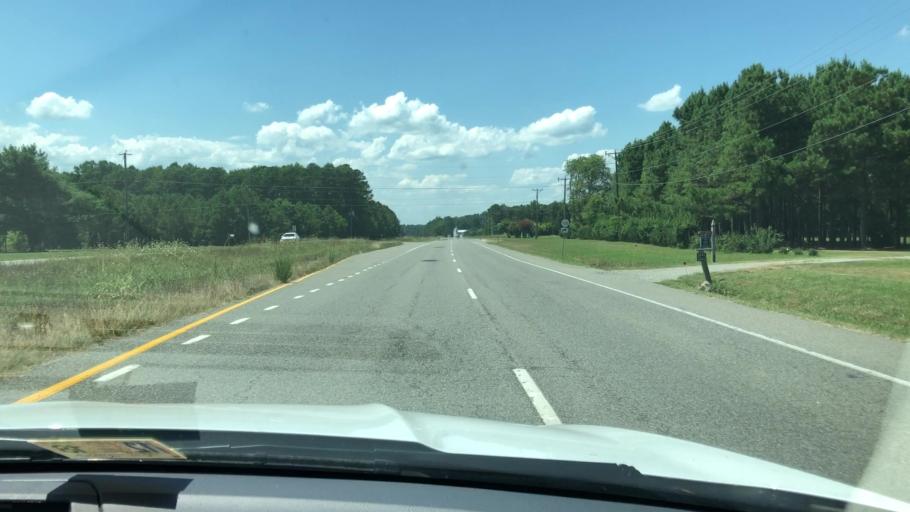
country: US
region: Virginia
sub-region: Middlesex County
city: Saluda
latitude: 37.6040
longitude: -76.5331
